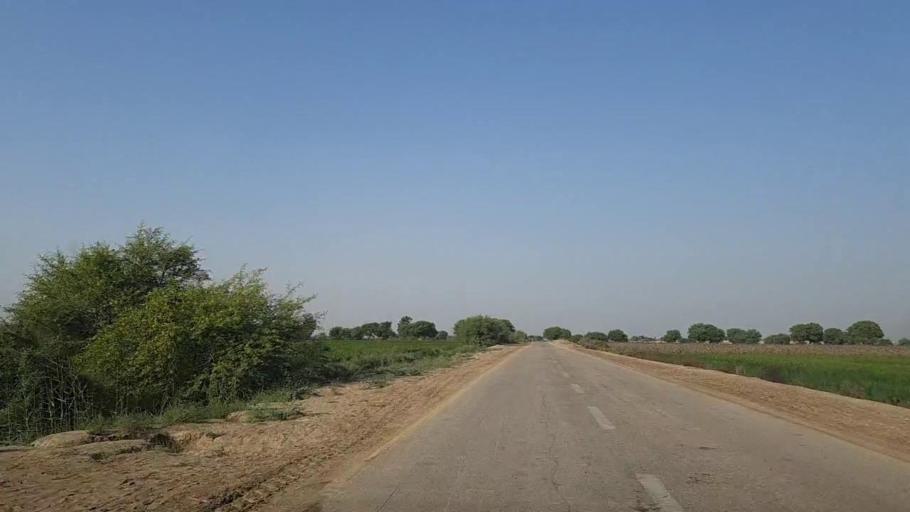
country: PK
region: Sindh
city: Mirpur Batoro
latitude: 24.5745
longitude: 68.3944
